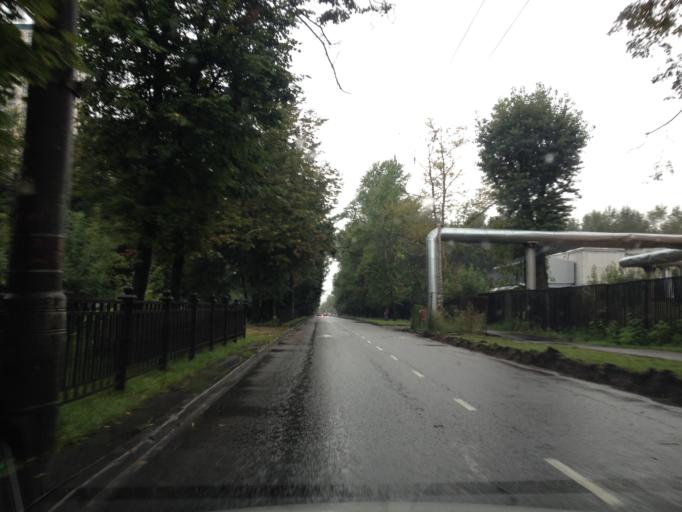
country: RU
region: Moskovskaya
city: Izmaylovo
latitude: 55.7972
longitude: 37.8111
